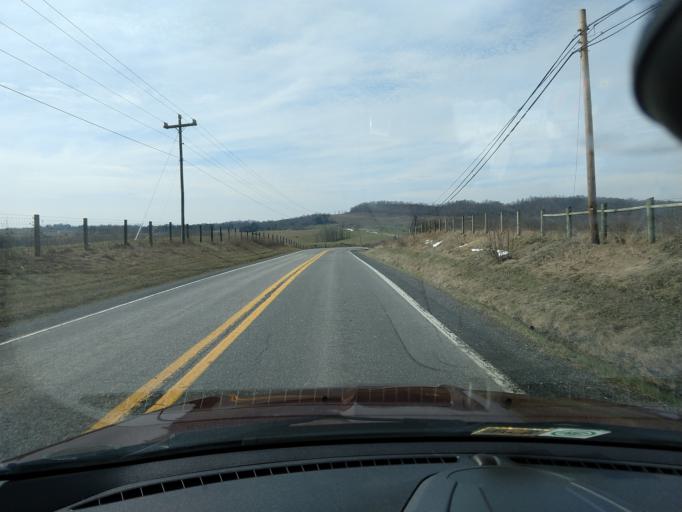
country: US
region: West Virginia
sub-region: Greenbrier County
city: Lewisburg
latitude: 37.8968
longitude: -80.4059
